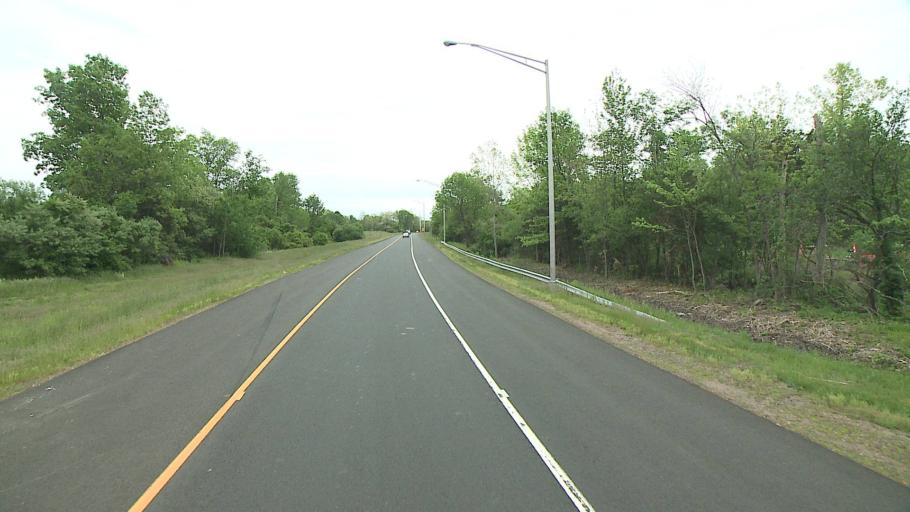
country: US
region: Connecticut
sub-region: Hartford County
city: West Hartford
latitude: 41.7256
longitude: -72.7797
